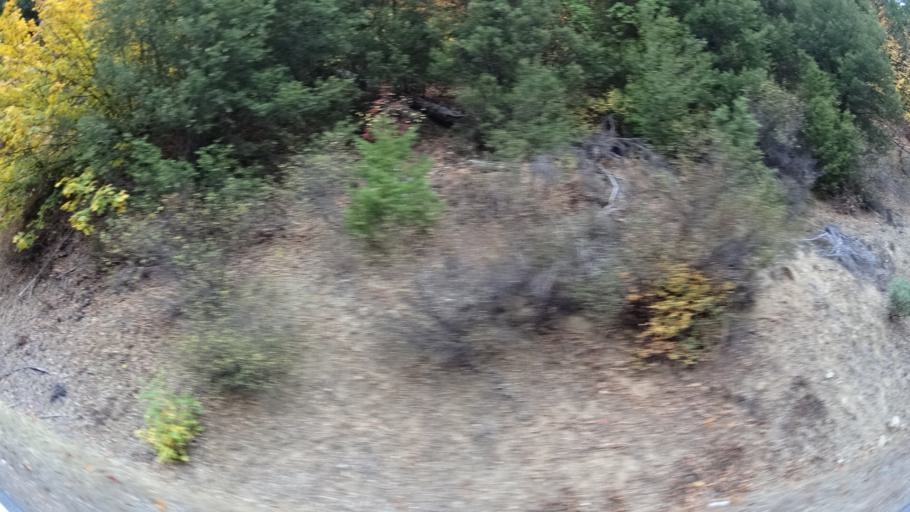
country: US
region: California
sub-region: Siskiyou County
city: Happy Camp
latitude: 41.9097
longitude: -123.4473
